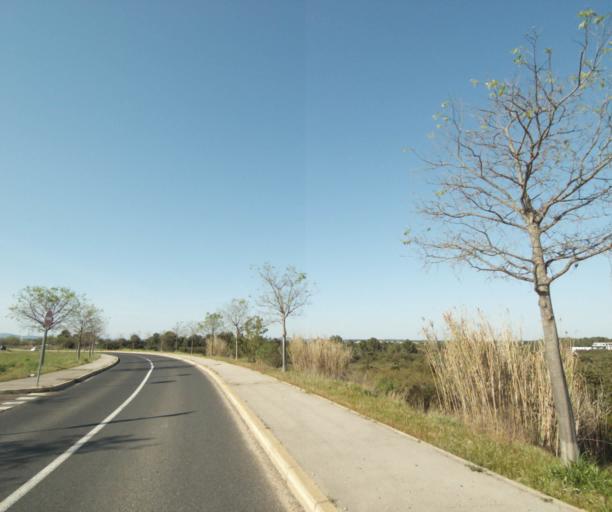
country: FR
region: Languedoc-Roussillon
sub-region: Departement de l'Herault
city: Jacou
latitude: 43.6492
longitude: 3.9231
